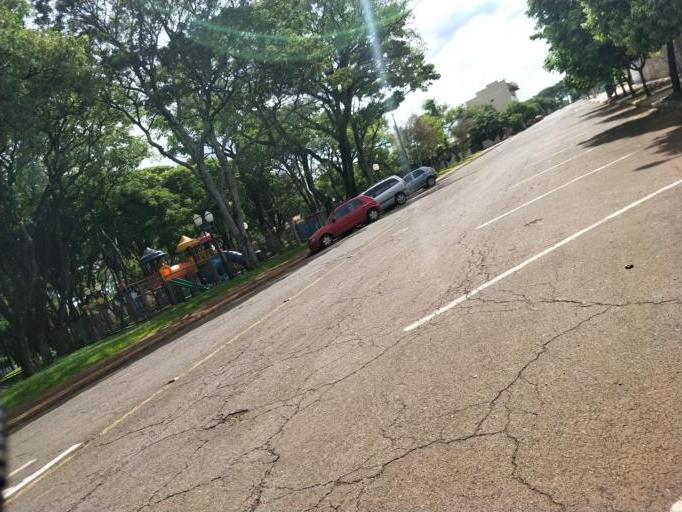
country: BR
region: Parana
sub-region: Marechal Candido Rondon
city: Marechal Candido Rondon
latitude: -24.5619
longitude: -54.0547
